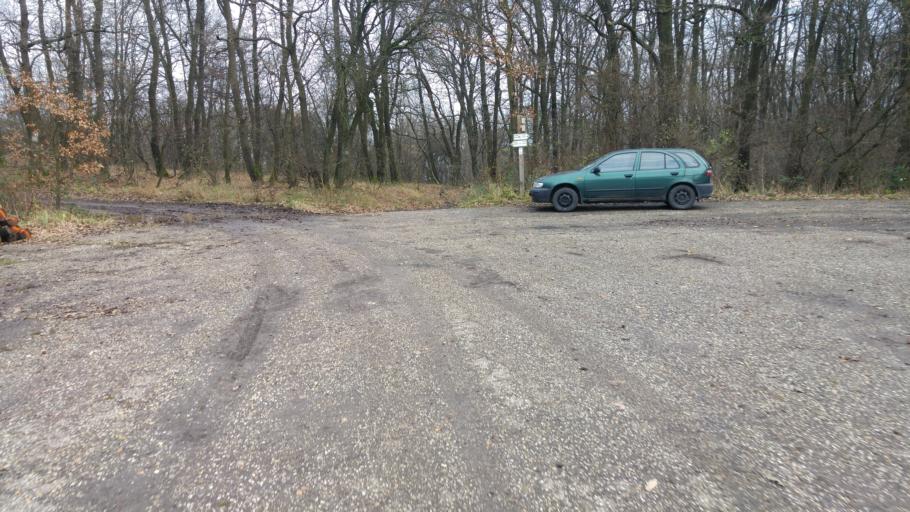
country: HU
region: Pest
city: Nagymaros
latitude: 47.8129
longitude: 18.9545
